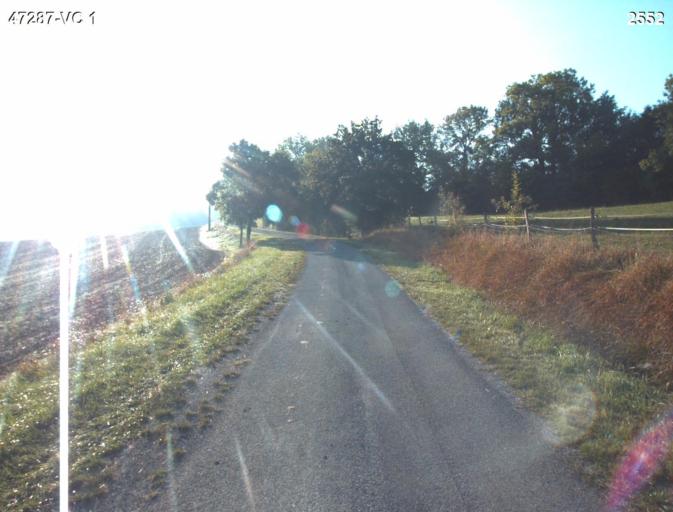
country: FR
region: Aquitaine
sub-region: Departement du Lot-et-Garonne
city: Sainte-Colombe-en-Bruilhois
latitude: 44.1428
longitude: 0.4439
